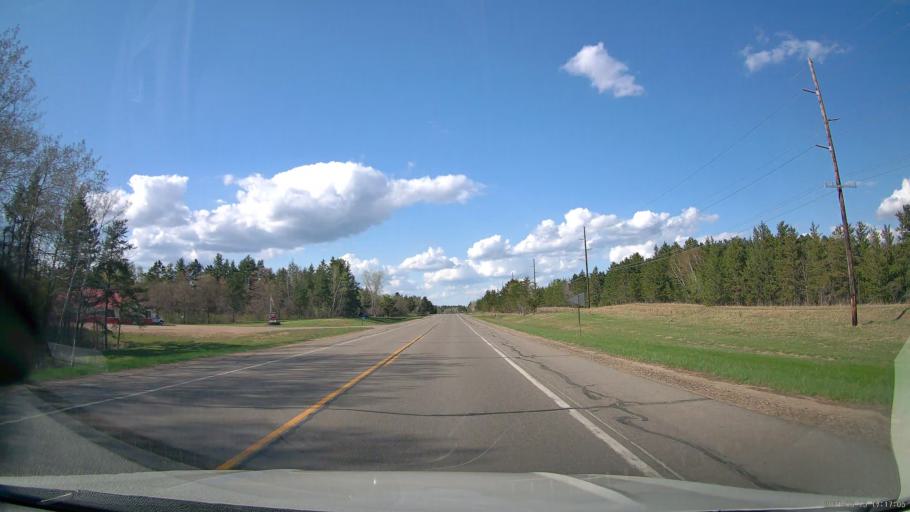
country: US
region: Minnesota
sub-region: Hubbard County
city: Park Rapids
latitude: 46.9390
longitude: -95.0167
